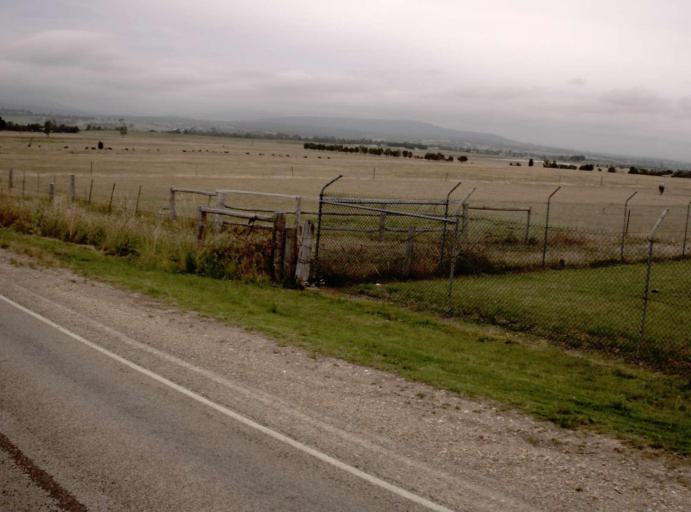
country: AU
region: Victoria
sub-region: East Gippsland
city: Bairnsdale
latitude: -37.8154
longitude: 147.4366
